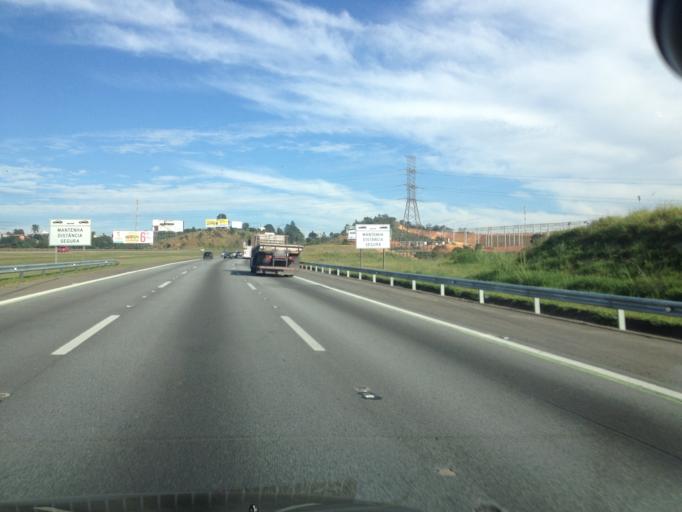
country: BR
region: Sao Paulo
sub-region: Mairinque
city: Mairinque
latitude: -23.4226
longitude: -47.2359
